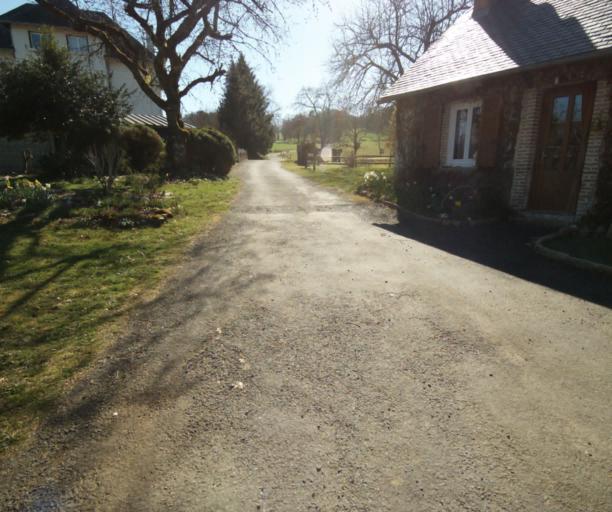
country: FR
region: Limousin
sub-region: Departement de la Correze
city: Chamboulive
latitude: 45.4114
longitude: 1.6714
